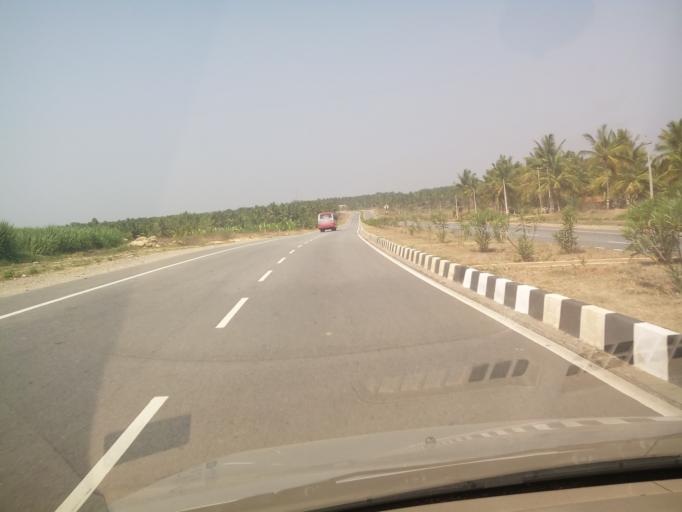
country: IN
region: Karnataka
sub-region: Hassan
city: Shravanabelagola
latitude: 12.9172
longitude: 76.4648
